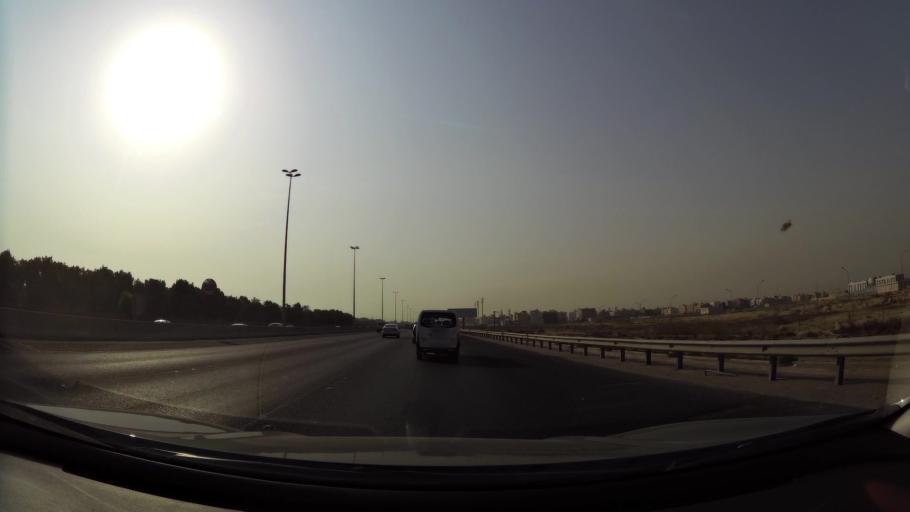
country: KW
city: Al Funaytis
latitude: 29.2442
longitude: 48.0930
